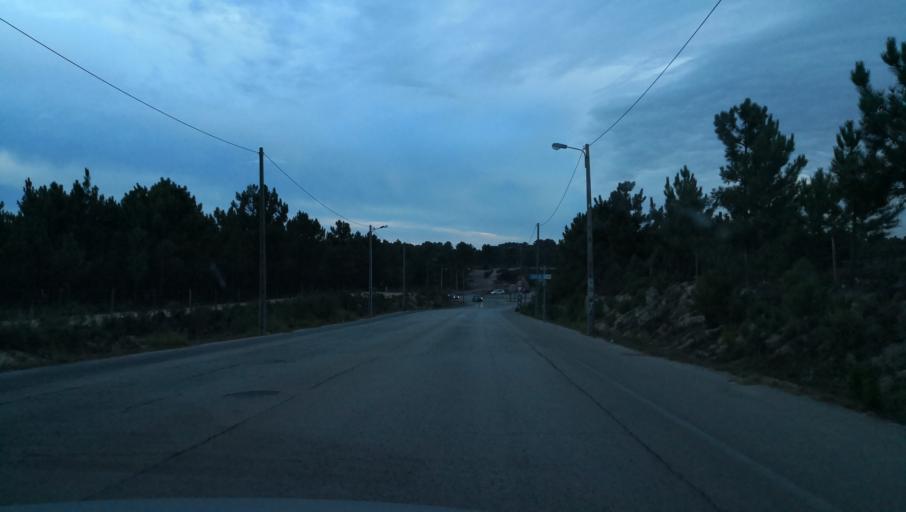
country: PT
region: Setubal
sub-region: Almada
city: Charneca
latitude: 38.5965
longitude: -9.1601
